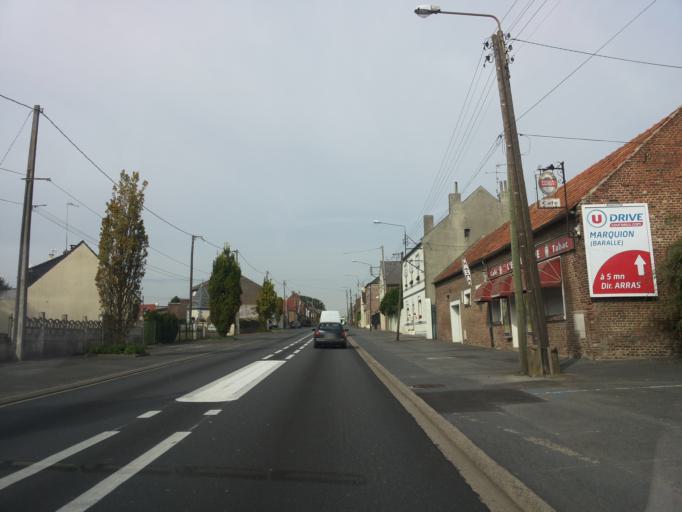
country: FR
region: Nord-Pas-de-Calais
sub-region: Departement du Nord
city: Raillencourt-Sainte-Olle
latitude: 50.1894
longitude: 3.1713
